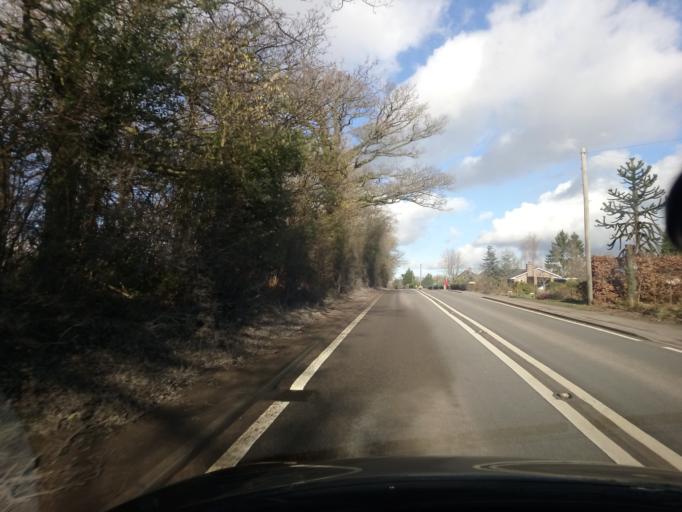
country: GB
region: England
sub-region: Shropshire
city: Astley
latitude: 52.7571
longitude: -2.7165
